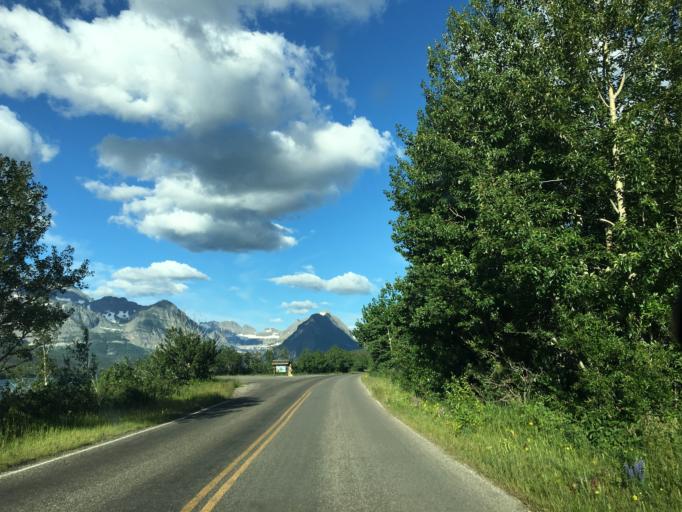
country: CA
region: Alberta
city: Cardston
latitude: 48.8246
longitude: -113.5693
